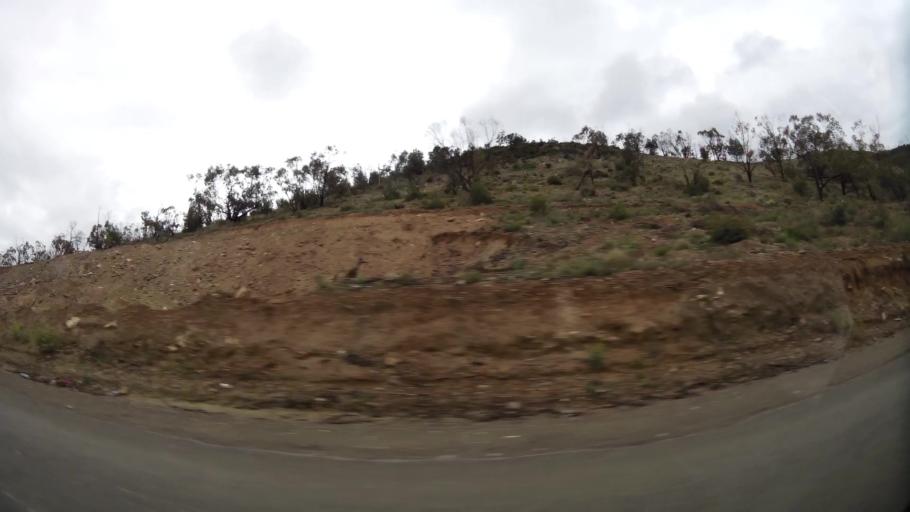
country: MA
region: Taza-Al Hoceima-Taounate
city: Imzourene
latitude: 34.9398
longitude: -3.8082
